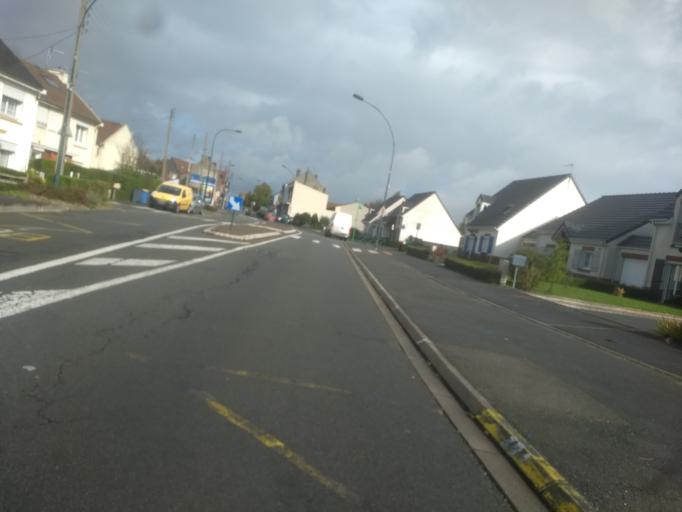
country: FR
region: Nord-Pas-de-Calais
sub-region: Departement du Pas-de-Calais
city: Achicourt
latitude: 50.2731
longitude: 2.7747
